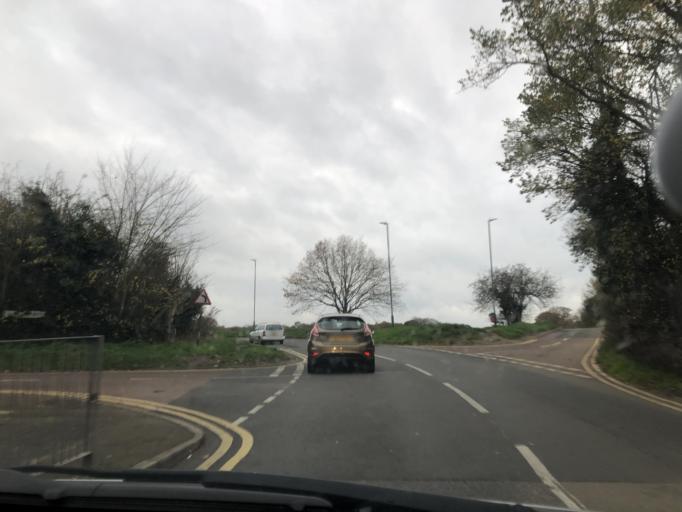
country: GB
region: England
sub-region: Greater London
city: Bexley
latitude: 51.4435
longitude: 0.1806
